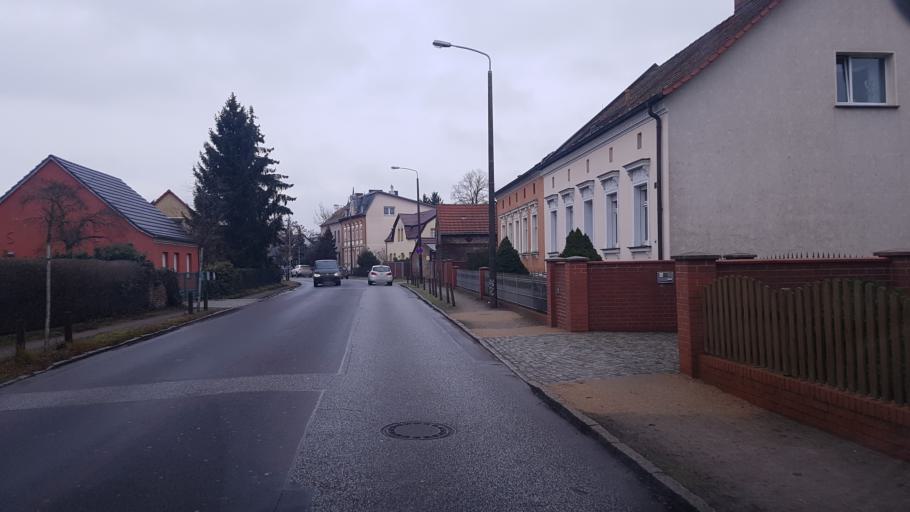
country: DE
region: Berlin
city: Wannsee
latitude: 52.3624
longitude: 13.1271
